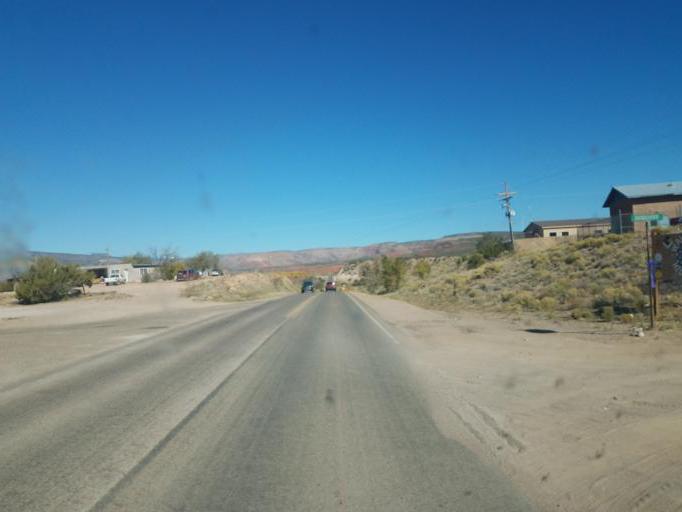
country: US
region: New Mexico
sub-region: Sandoval County
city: Jemez Pueblo
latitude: 35.6201
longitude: -106.7238
